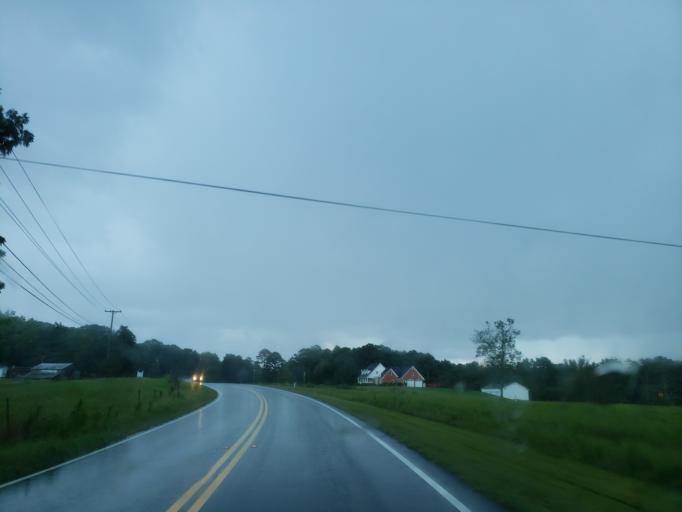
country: US
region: Georgia
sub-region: Cherokee County
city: Canton
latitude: 34.3042
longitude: -84.4572
